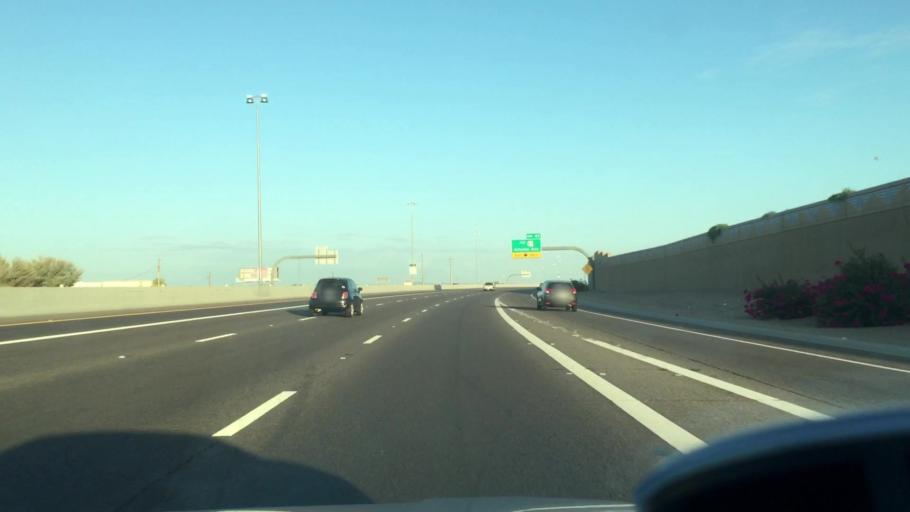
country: US
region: Arizona
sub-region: Maricopa County
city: Chandler
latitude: 33.2838
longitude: -111.8290
